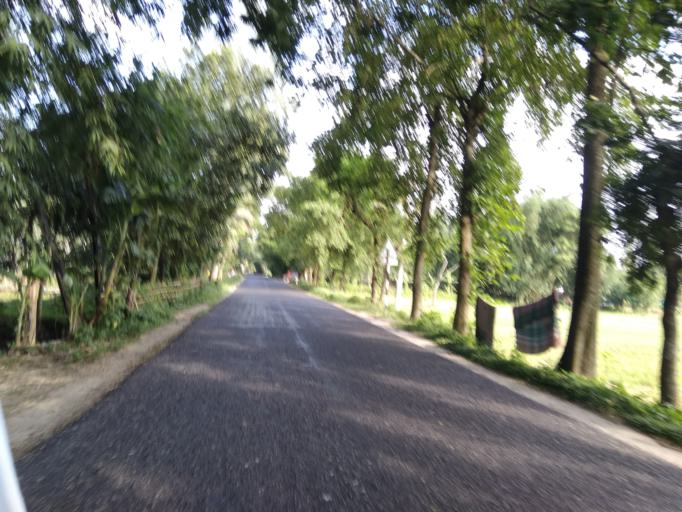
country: BD
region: Rangpur Division
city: Rangpur
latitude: 25.8338
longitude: 89.1165
